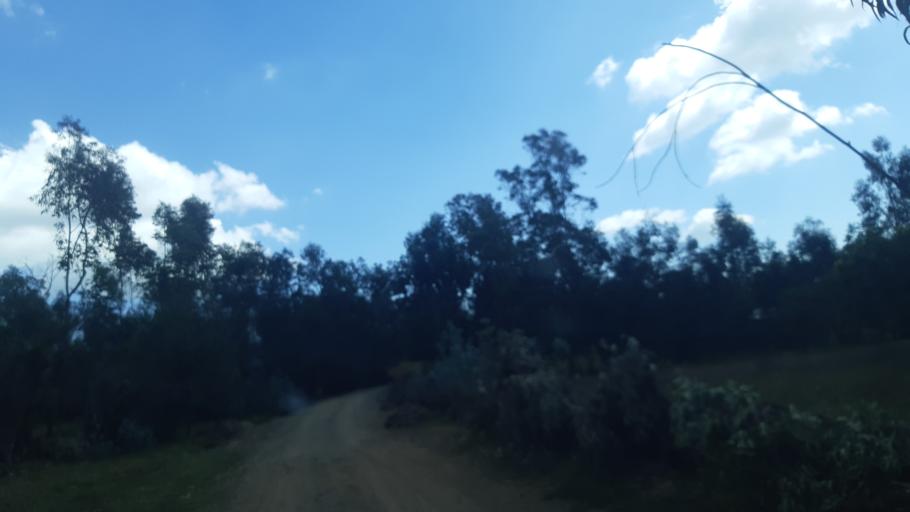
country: ET
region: Amhara
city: Dabat
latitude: 13.3563
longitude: 37.3873
